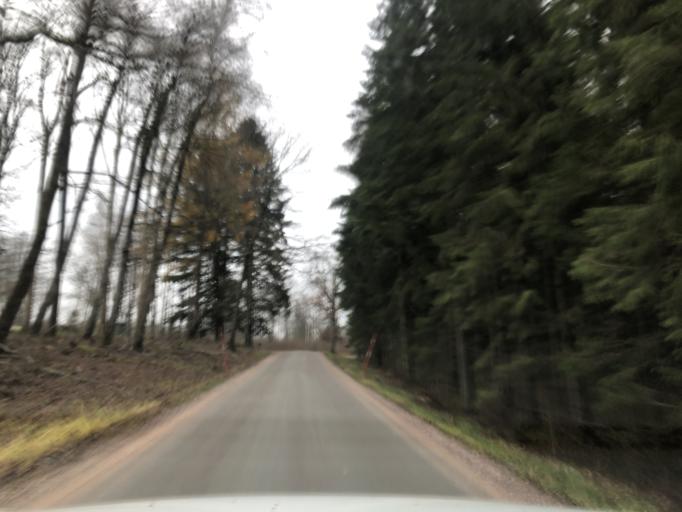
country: SE
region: Vaestra Goetaland
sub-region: Ulricehamns Kommun
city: Ulricehamn
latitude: 57.8473
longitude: 13.6359
